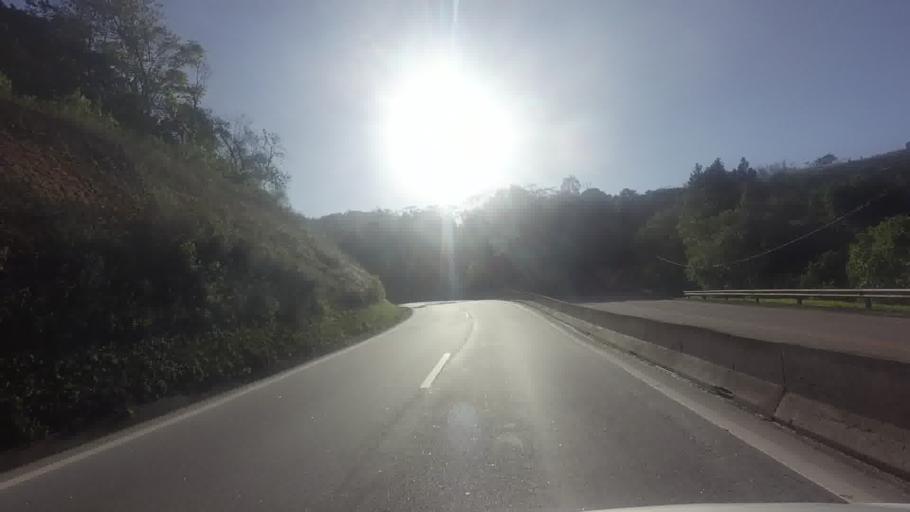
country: BR
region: Rio de Janeiro
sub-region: Petropolis
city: Petropolis
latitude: -22.6015
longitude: -43.2815
